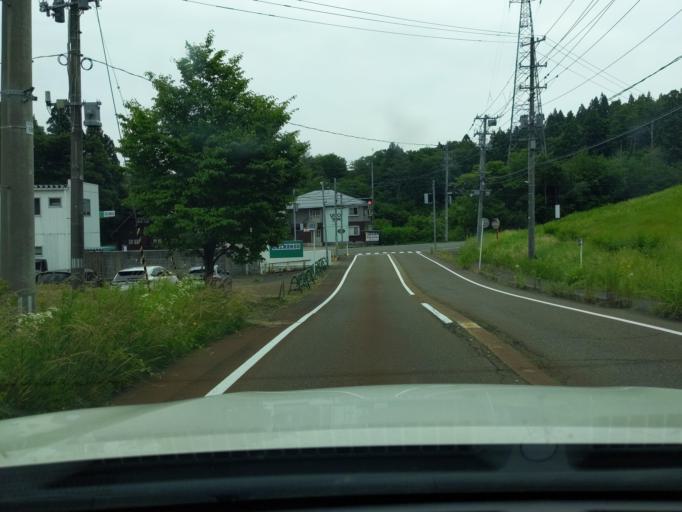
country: JP
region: Niigata
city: Kashiwazaki
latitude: 37.3474
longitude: 138.5991
